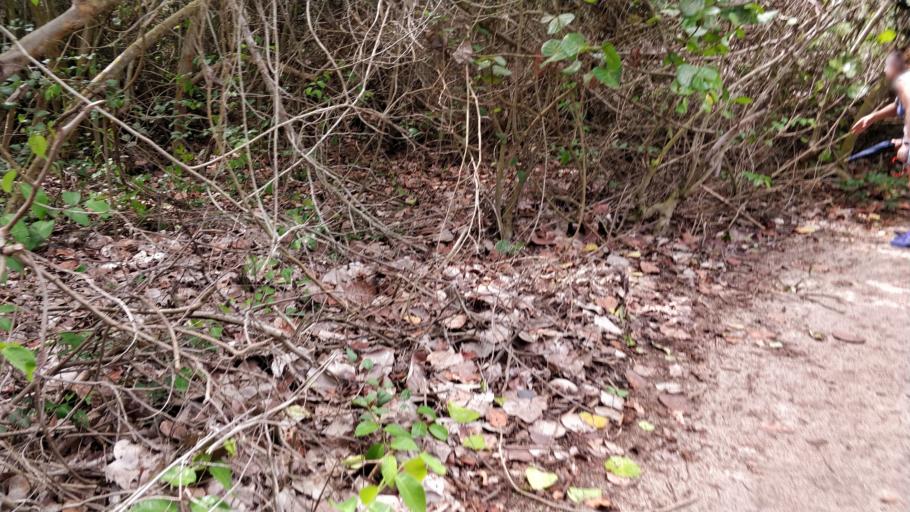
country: CO
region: Magdalena
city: Santa Marta
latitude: 11.3117
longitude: -73.9395
